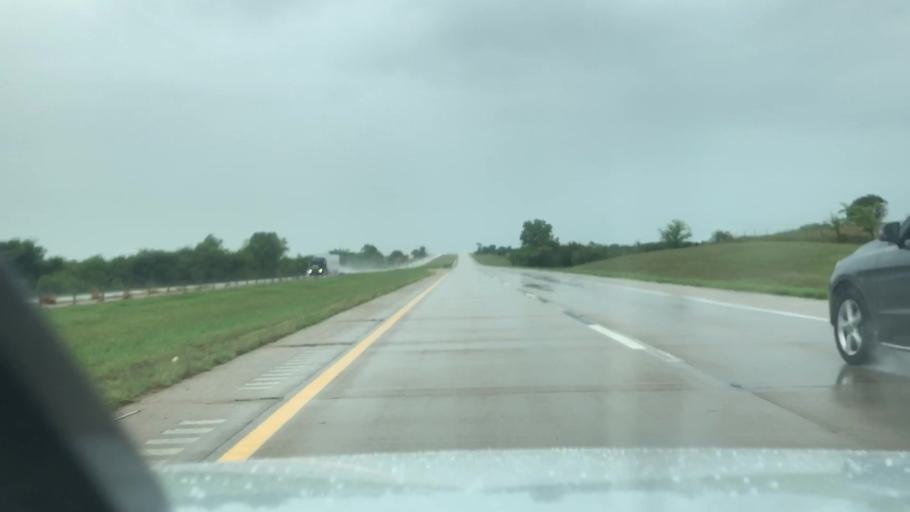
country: US
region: Oklahoma
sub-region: Osage County
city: Skiatook
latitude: 36.4077
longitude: -95.9204
